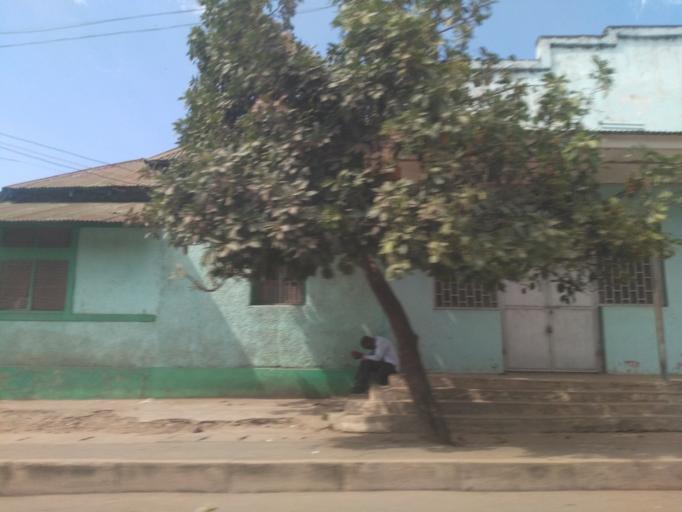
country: TZ
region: Mwanza
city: Mwanza
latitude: -2.5159
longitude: 32.9017
